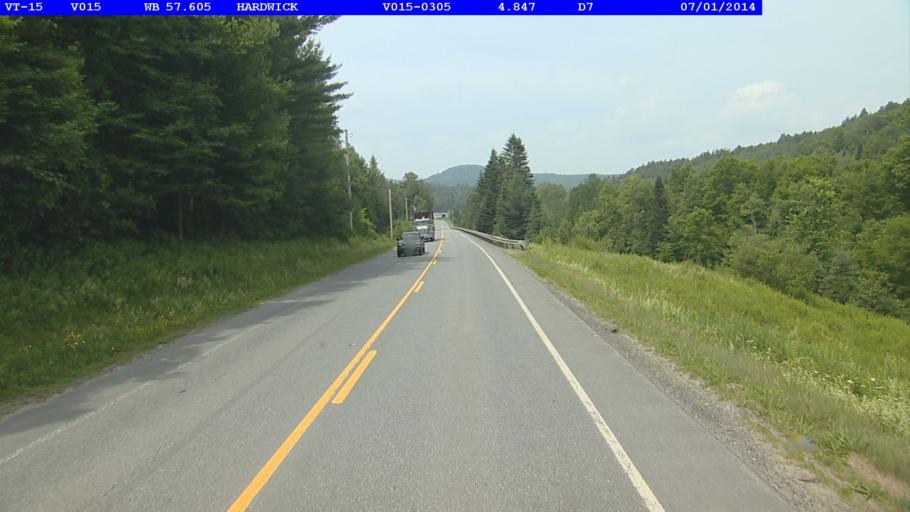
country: US
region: Vermont
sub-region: Caledonia County
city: Hardwick
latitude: 44.5029
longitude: -72.3400
